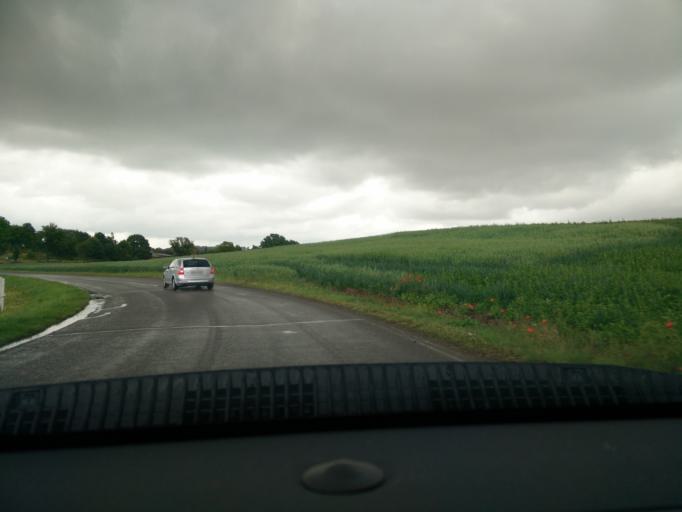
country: DE
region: Saxony
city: Nerchau
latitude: 51.2551
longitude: 12.7589
